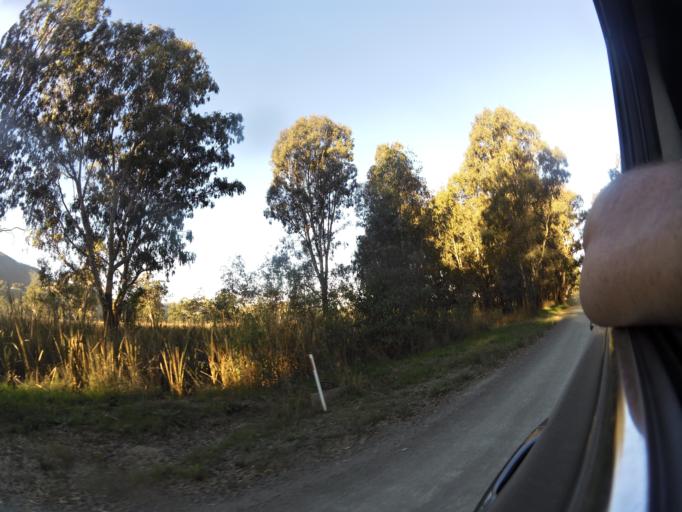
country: AU
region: Victoria
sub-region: Murrindindi
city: Alexandra
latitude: -37.1607
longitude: 145.5446
